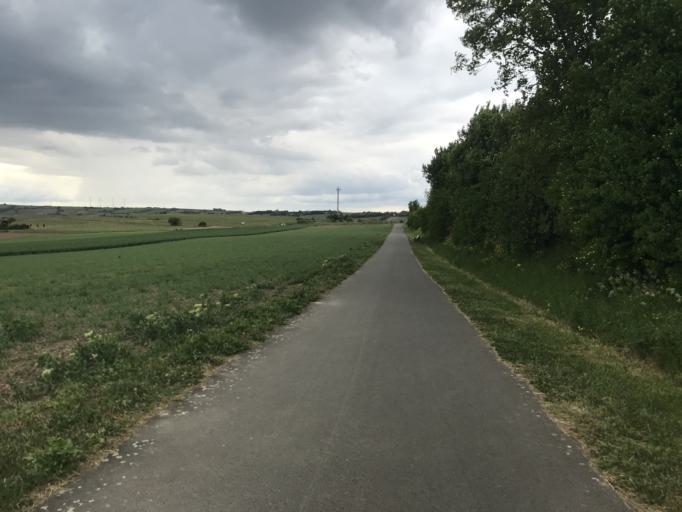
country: DE
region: Rheinland-Pfalz
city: Lorzweiler
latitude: 49.9004
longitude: 8.2900
